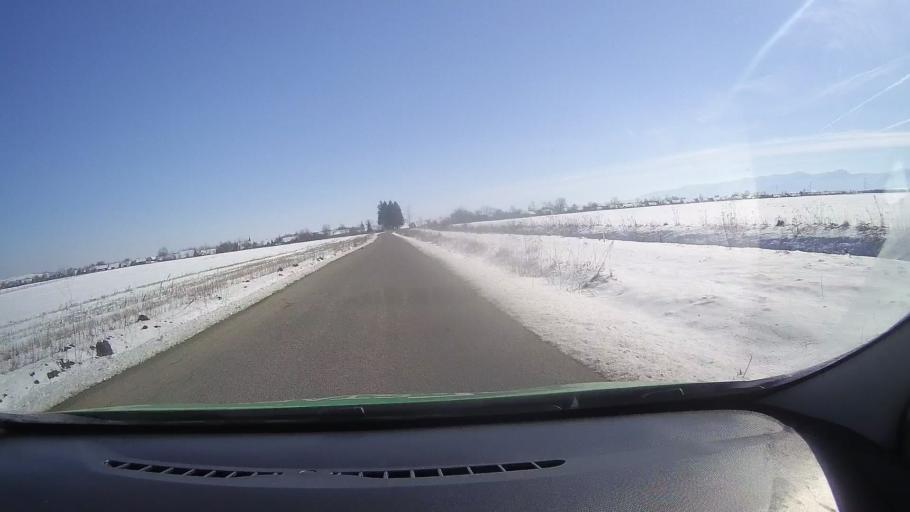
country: RO
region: Brasov
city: Fogarasch
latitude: 45.8167
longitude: 24.9968
